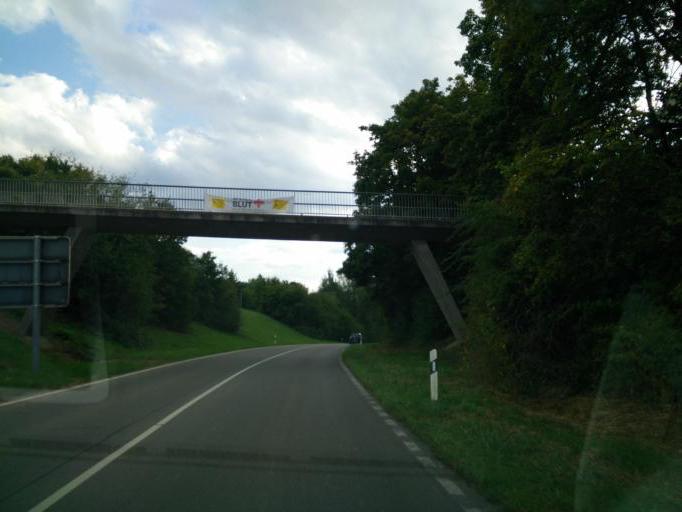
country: DE
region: Baden-Wuerttemberg
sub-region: Tuebingen Region
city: Kirchentellinsfurt
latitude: 48.5295
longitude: 9.1580
